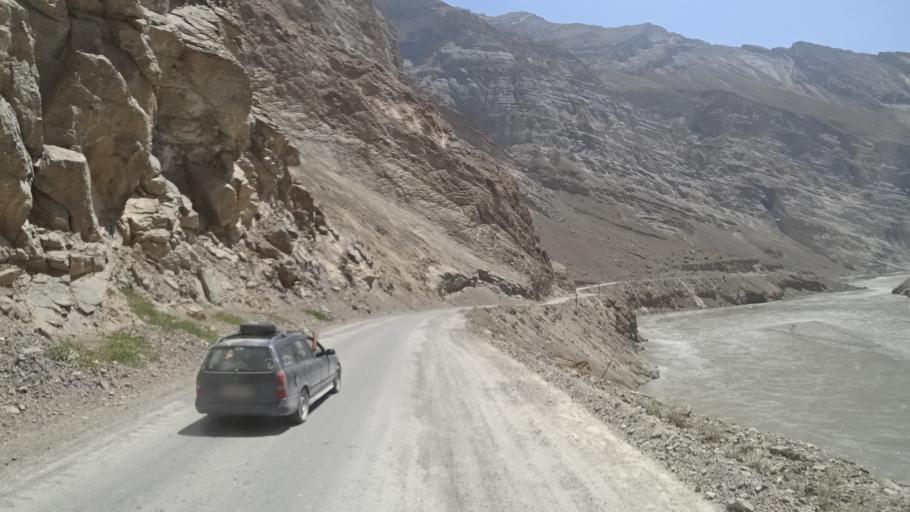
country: TJ
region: Gorno-Badakhshan
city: Vanj
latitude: 38.2205
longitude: 71.3707
